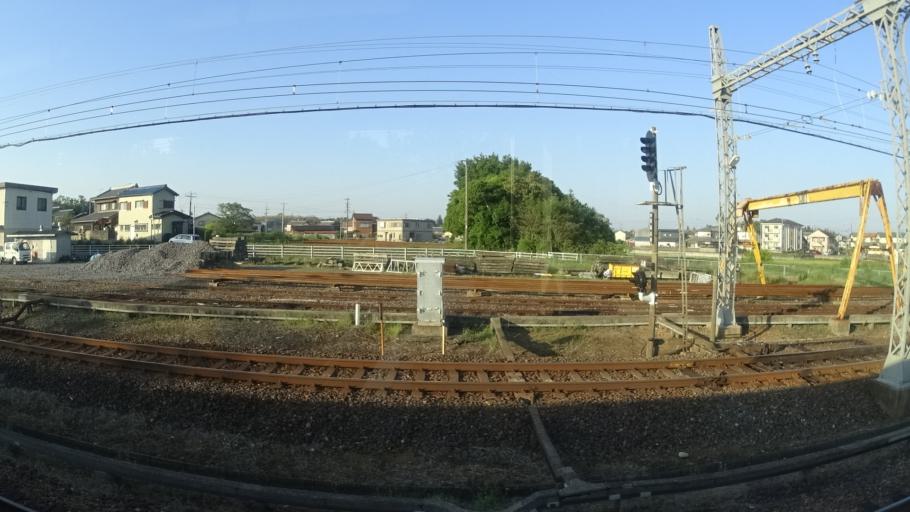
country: JP
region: Mie
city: Ise
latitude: 34.5319
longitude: 136.6412
